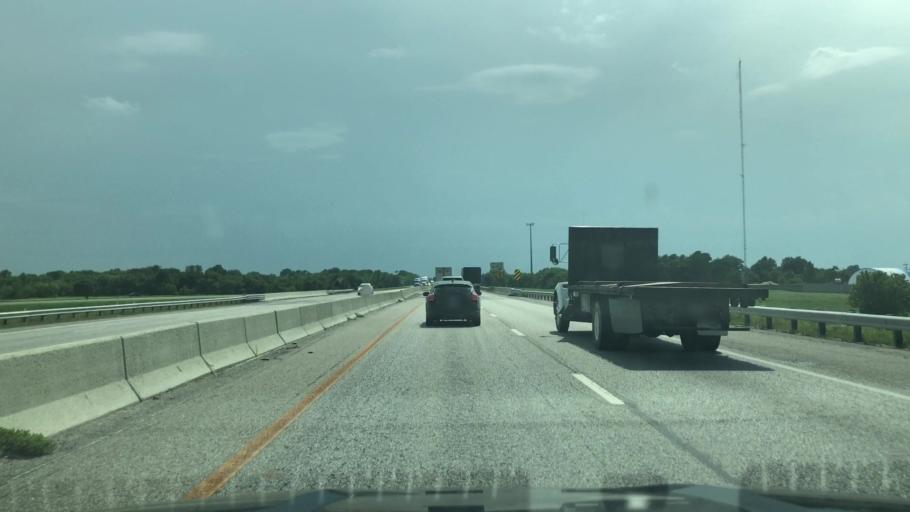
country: US
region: Oklahoma
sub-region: Craig County
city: Vinita
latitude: 36.6334
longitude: -95.1321
